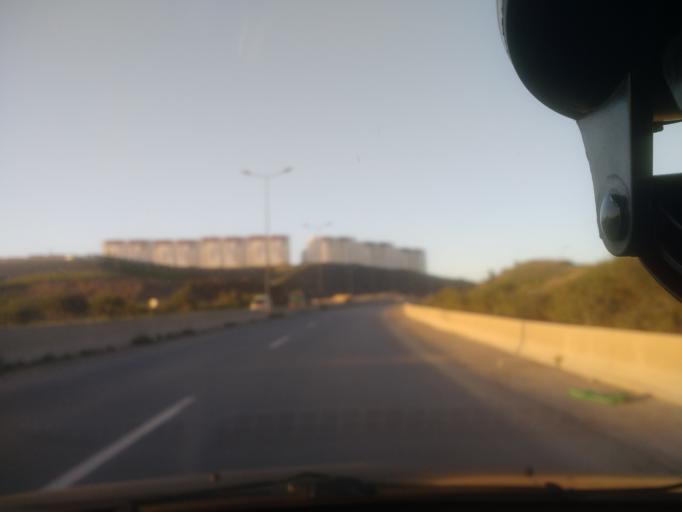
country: DZ
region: Boumerdes
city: Draa Ben Khedda
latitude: 36.7283
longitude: 3.9935
